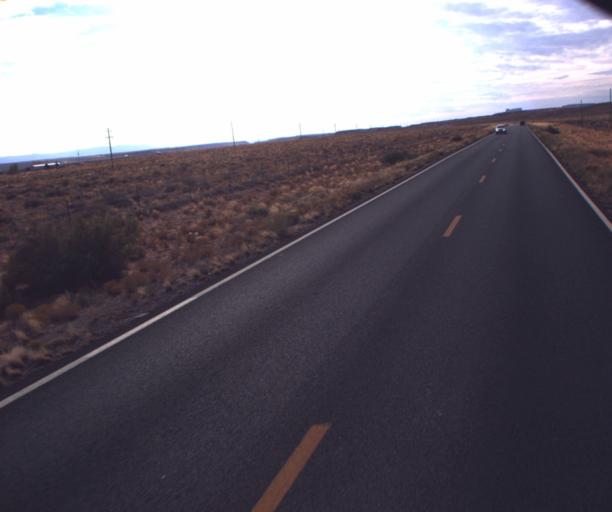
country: US
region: Arizona
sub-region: Apache County
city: Many Farms
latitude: 36.6204
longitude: -109.5815
